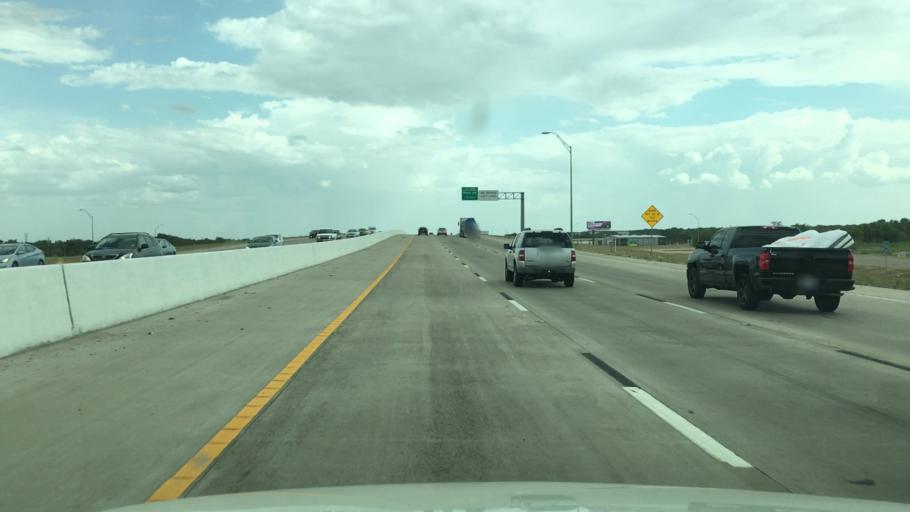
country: US
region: Texas
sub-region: McLennan County
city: West
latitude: 31.7312
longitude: -97.1032
